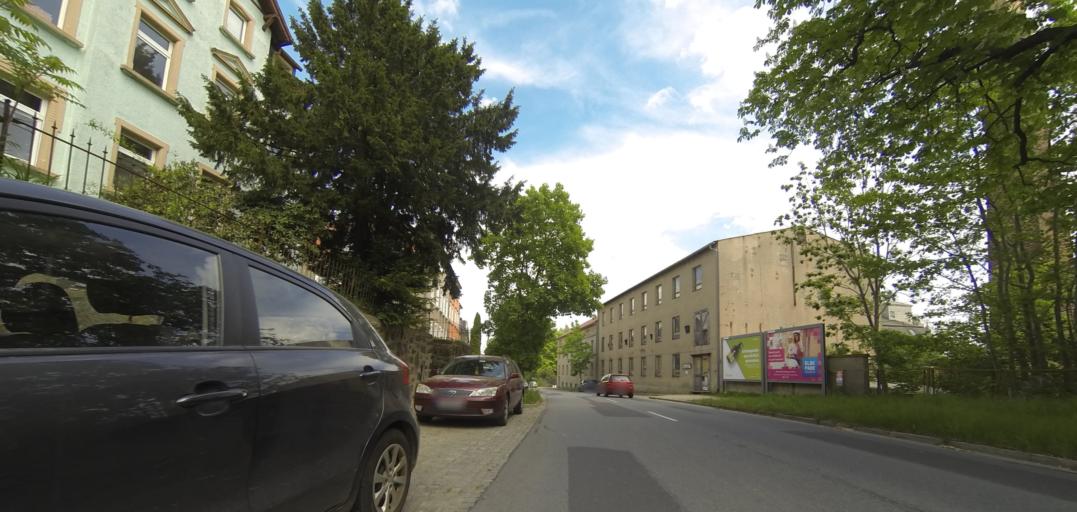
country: DE
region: Saxony
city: Bischofswerda
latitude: 51.1235
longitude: 14.1731
